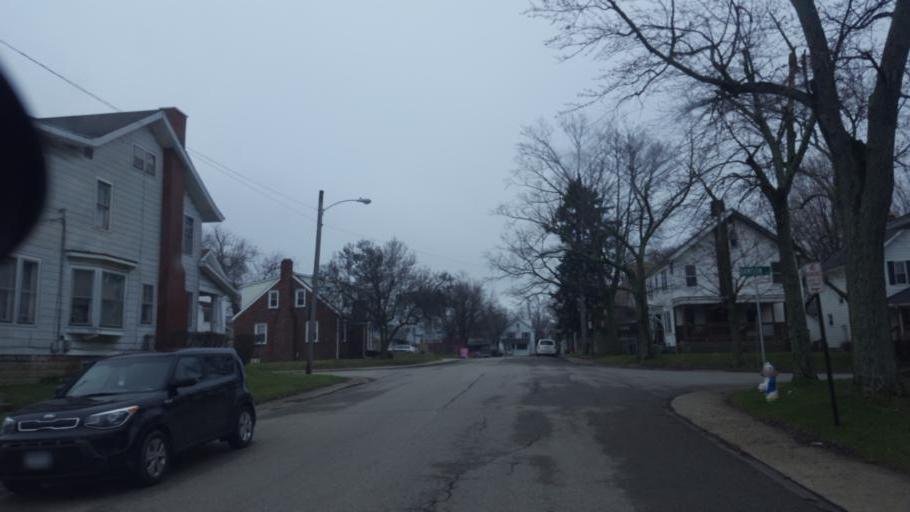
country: US
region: Ohio
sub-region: Richland County
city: Mansfield
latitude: 40.7576
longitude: -82.5358
